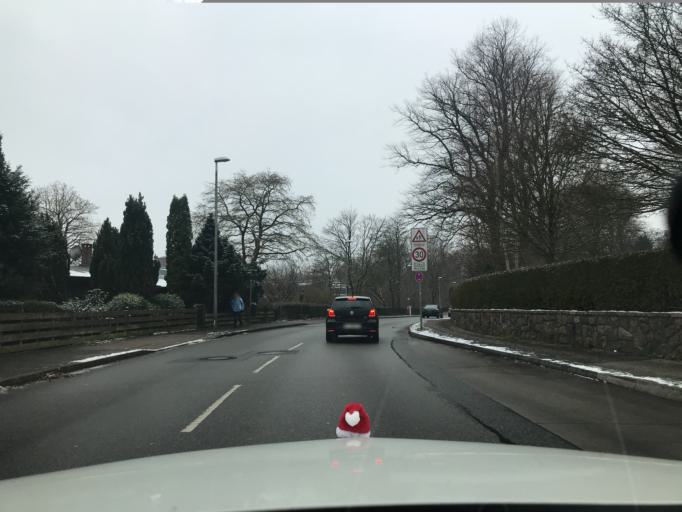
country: DE
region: Schleswig-Holstein
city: Flensburg
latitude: 54.7839
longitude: 9.4217
